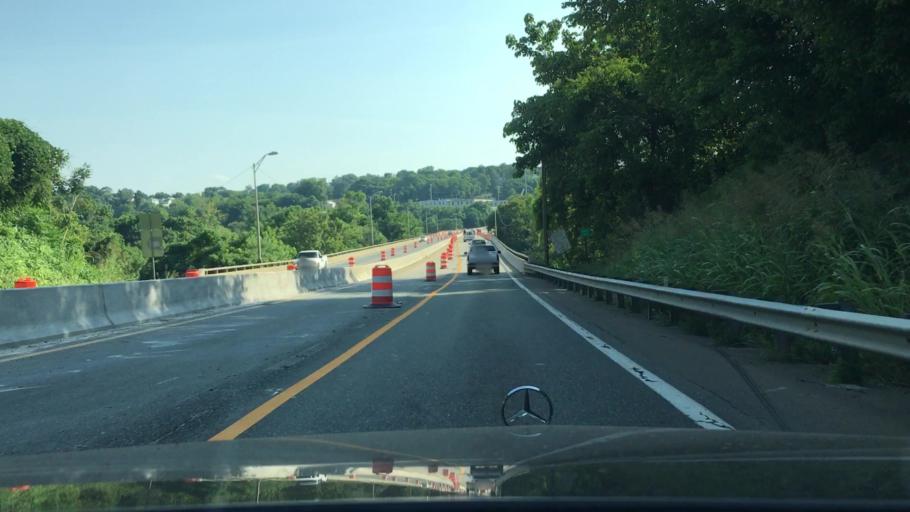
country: US
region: Virginia
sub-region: City of Lynchburg
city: Lynchburg
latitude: 37.4128
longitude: -79.1321
